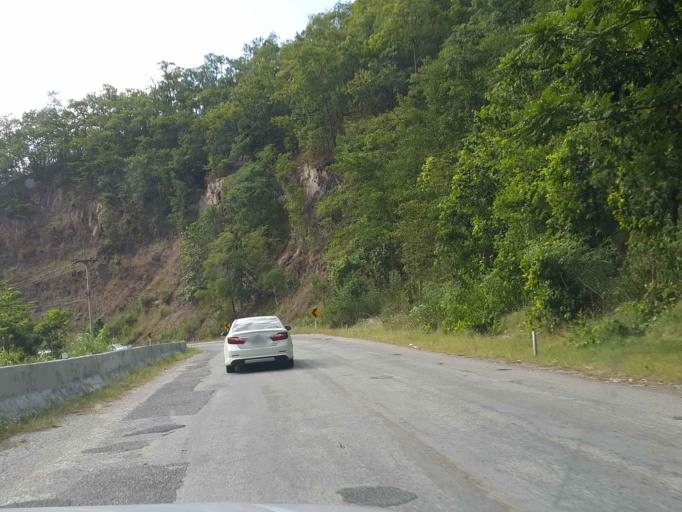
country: TH
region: Lampang
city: Thoen
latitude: 17.6383
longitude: 99.3087
